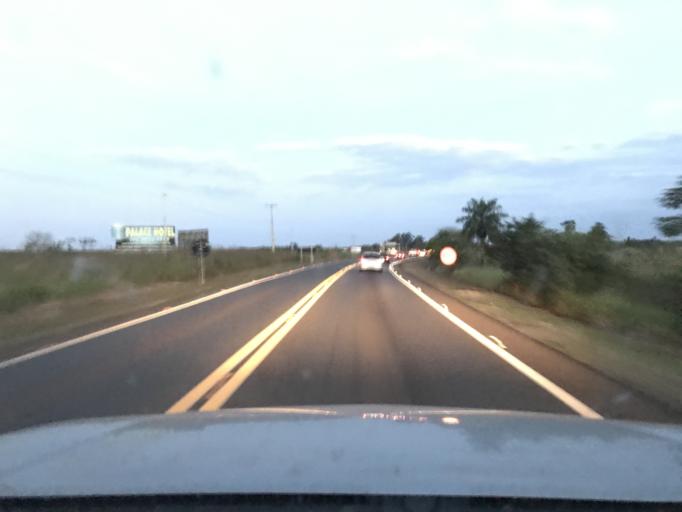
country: PY
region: Canindeyu
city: Salto del Guaira
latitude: -24.0369
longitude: -54.2816
